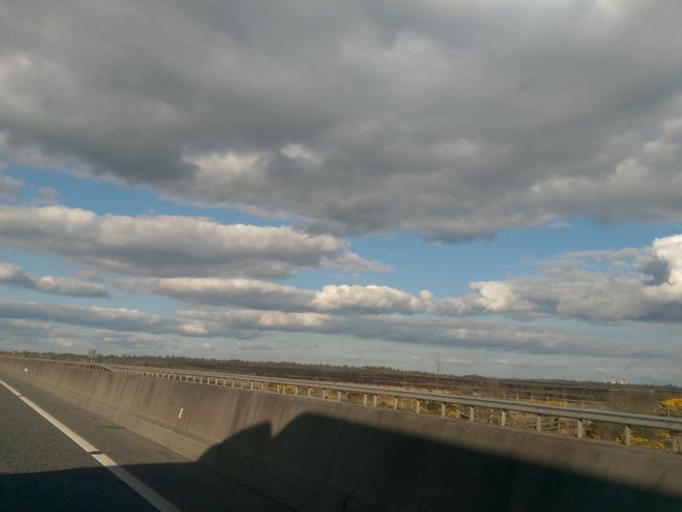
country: IE
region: Leinster
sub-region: An Iarmhi
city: Rochfortbridge
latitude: 53.4331
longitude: -7.2186
